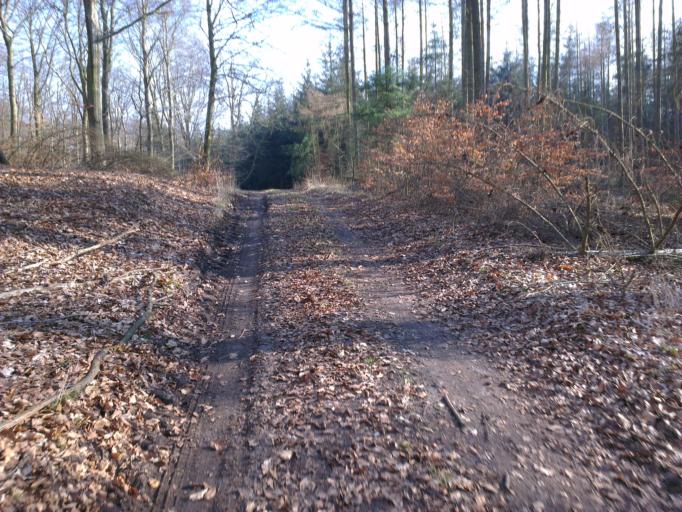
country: DK
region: Capital Region
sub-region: Frederikssund Kommune
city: Jaegerspris
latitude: 55.8946
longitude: 11.9997
